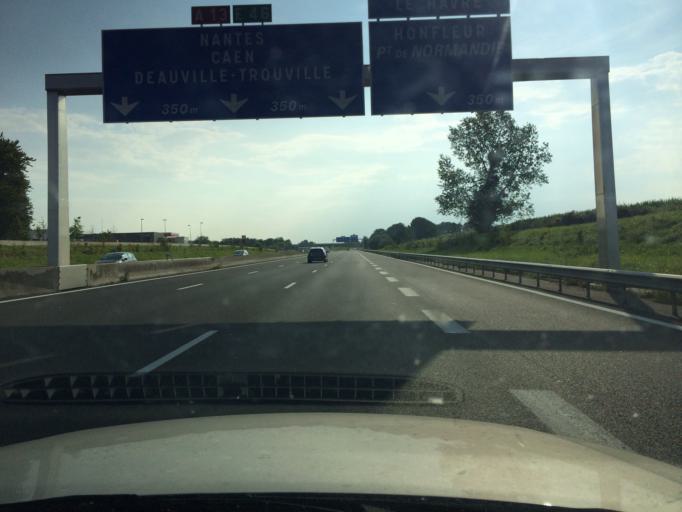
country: FR
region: Haute-Normandie
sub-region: Departement de l'Eure
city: Beuzeville
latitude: 49.3220
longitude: 0.3219
